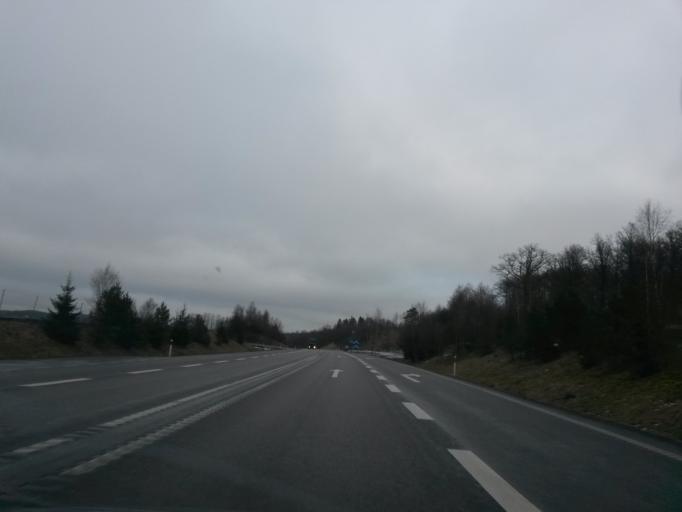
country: SE
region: Vaestra Goetaland
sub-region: Marks Kommun
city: Kinna
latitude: 57.4877
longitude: 12.6832
